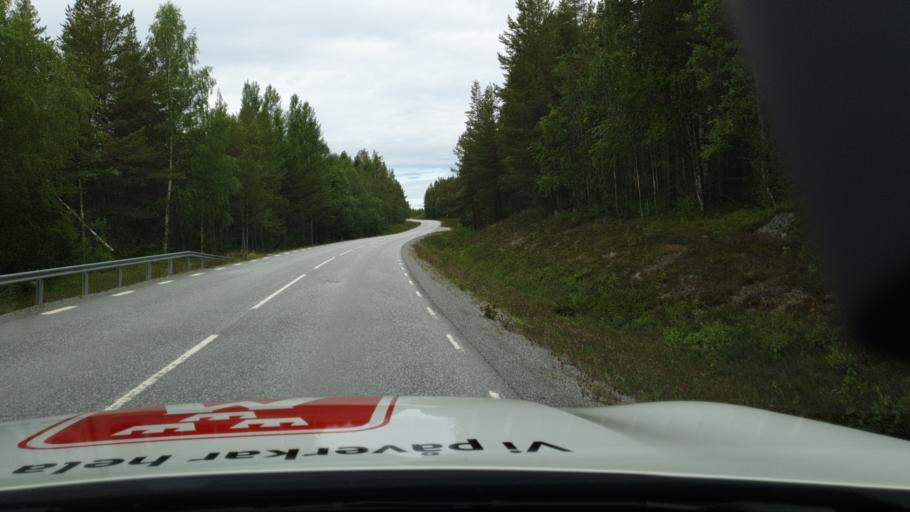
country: SE
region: Vaesterbotten
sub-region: Storumans Kommun
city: Storuman
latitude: 65.1627
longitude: 17.0407
